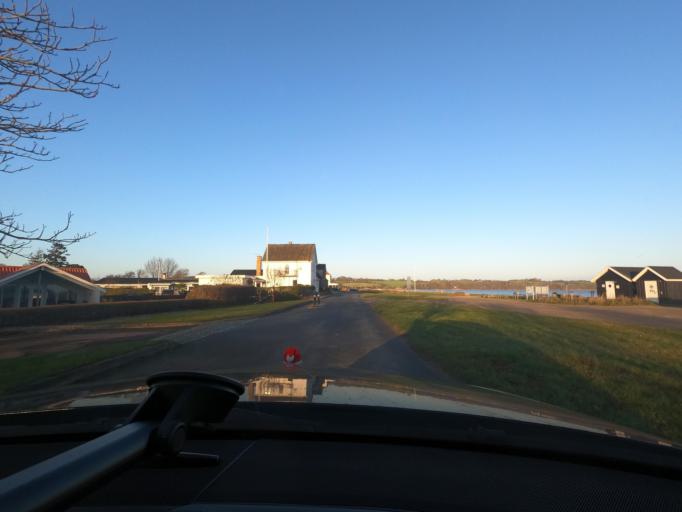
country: DK
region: South Denmark
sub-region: Sonderborg Kommune
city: Broager
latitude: 54.8953
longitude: 9.7004
